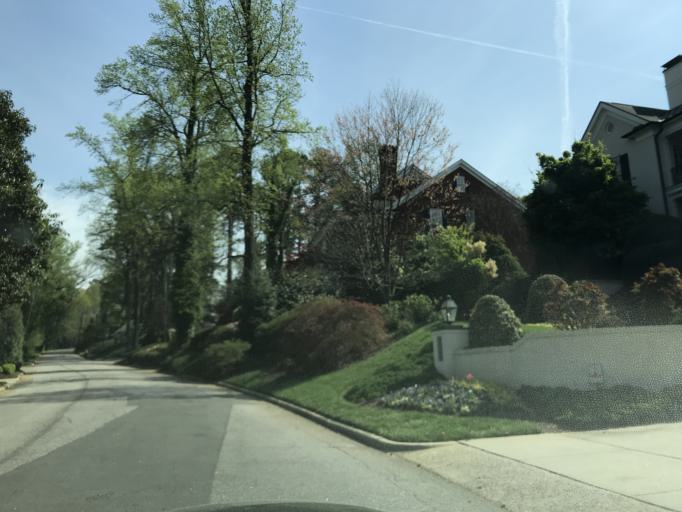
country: US
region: North Carolina
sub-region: Wake County
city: West Raleigh
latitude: 35.8074
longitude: -78.6611
